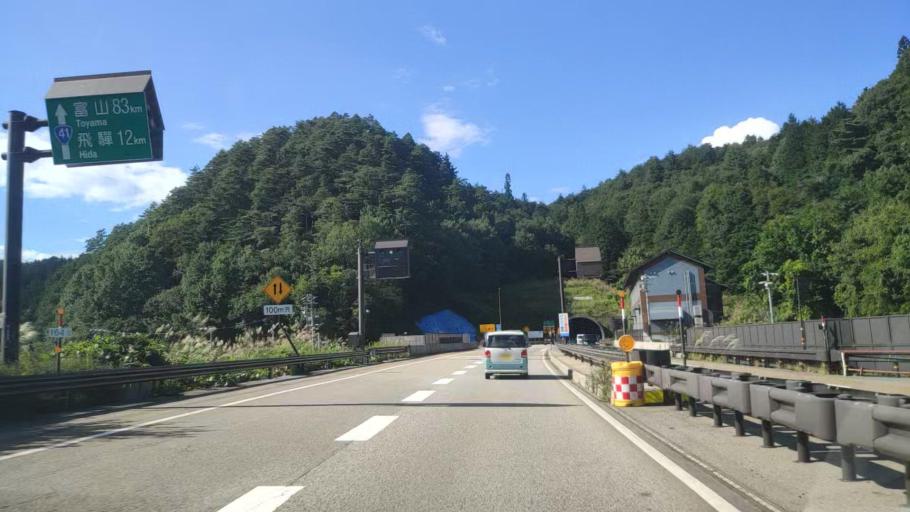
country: JP
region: Gifu
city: Takayama
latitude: 36.1703
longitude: 137.2260
